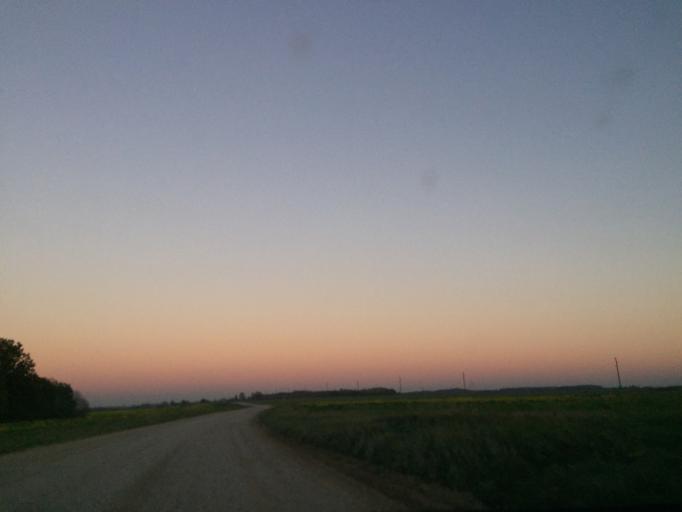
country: LT
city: Akmene
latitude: 56.3782
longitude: 22.6840
